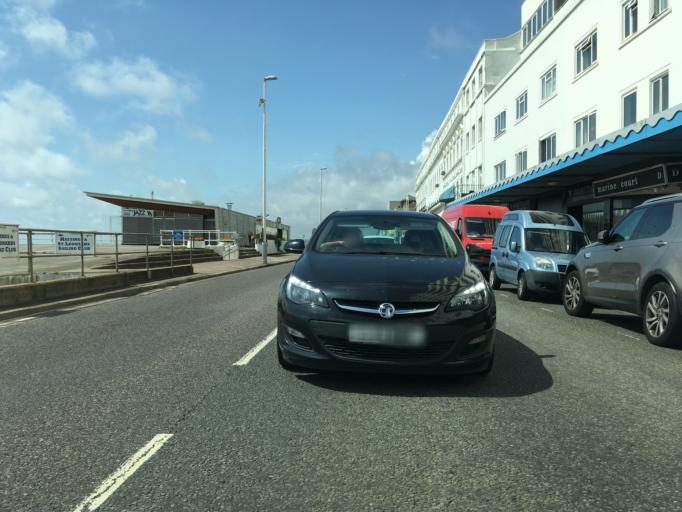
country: GB
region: England
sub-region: East Sussex
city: Saint Leonards-on-Sea
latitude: 50.8509
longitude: 0.5565
